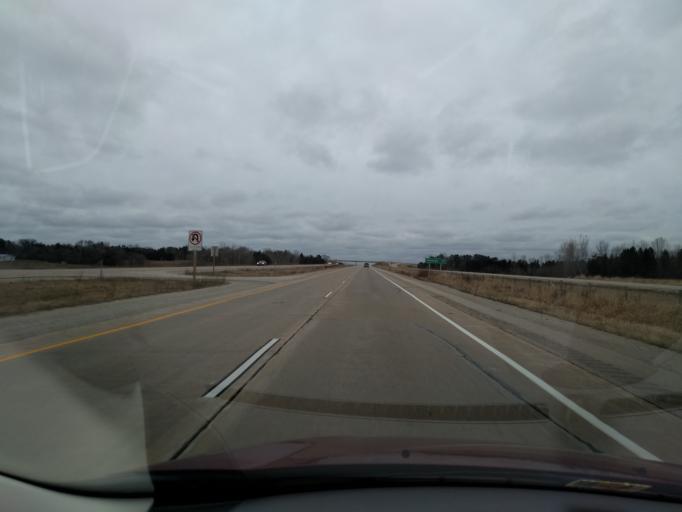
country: US
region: Wisconsin
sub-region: Winnebago County
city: Winneconne
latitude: 44.1898
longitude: -88.6713
